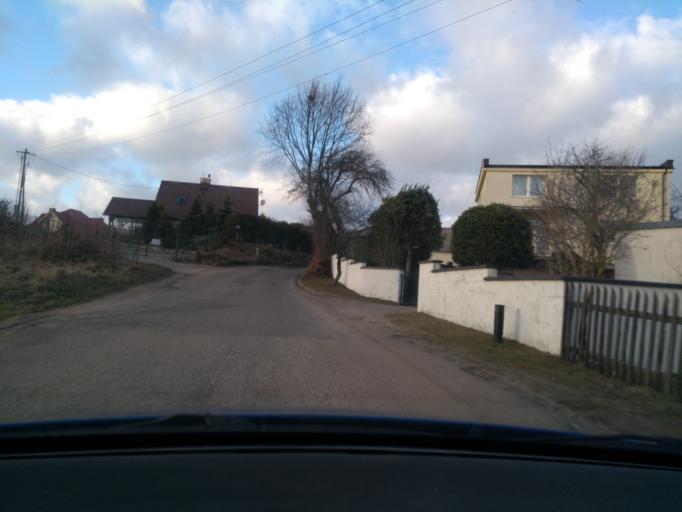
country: PL
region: Pomeranian Voivodeship
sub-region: Powiat kartuski
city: Kartuzy
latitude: 54.3732
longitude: 18.2158
